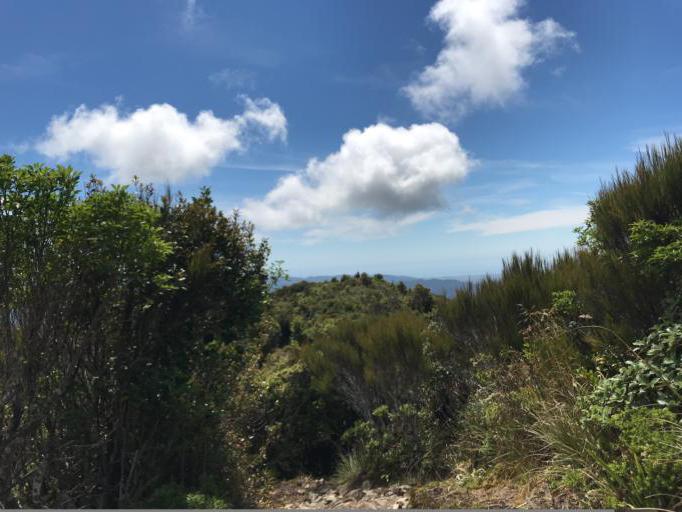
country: NZ
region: Wellington
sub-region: Kapiti Coast District
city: Otaki
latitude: -40.9096
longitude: 175.2595
